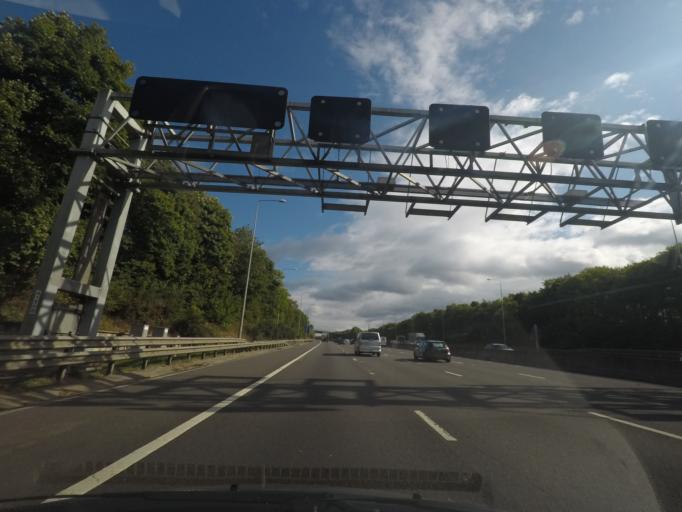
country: GB
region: England
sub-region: Derbyshire
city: Pinxton
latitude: 53.0838
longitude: -1.2986
